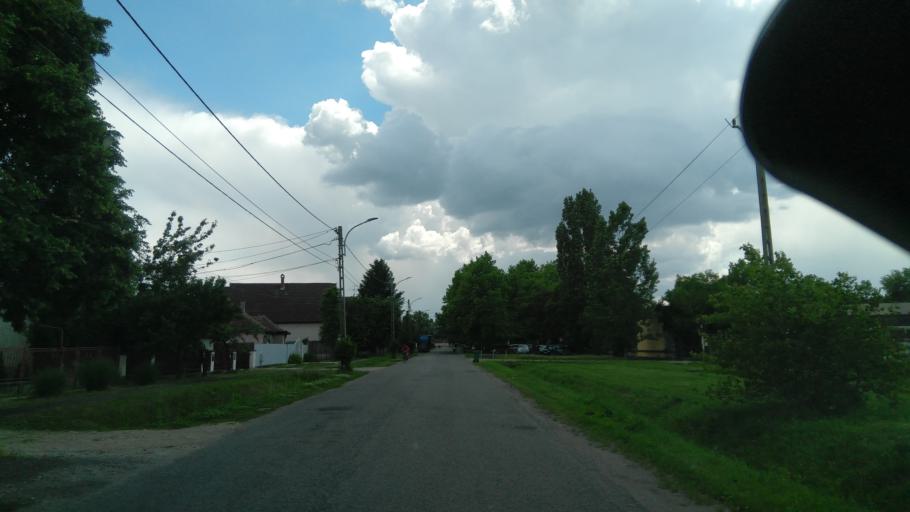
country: HU
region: Bekes
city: Gyula
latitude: 46.6605
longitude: 21.2696
